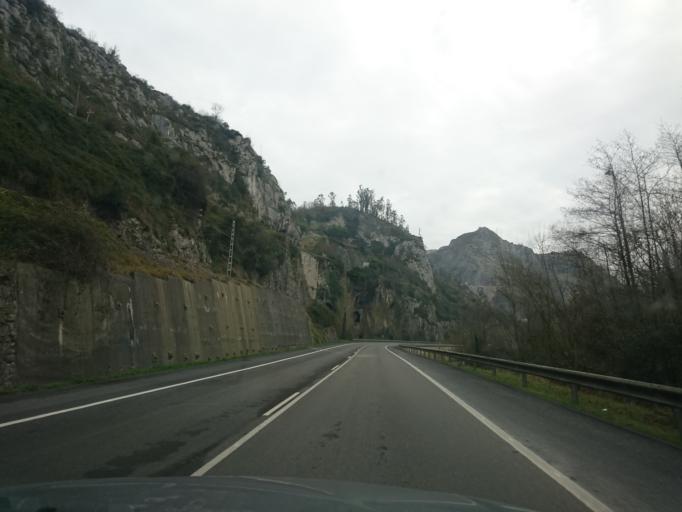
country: ES
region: Asturias
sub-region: Province of Asturias
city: Norena
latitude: 43.3341
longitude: -5.7627
